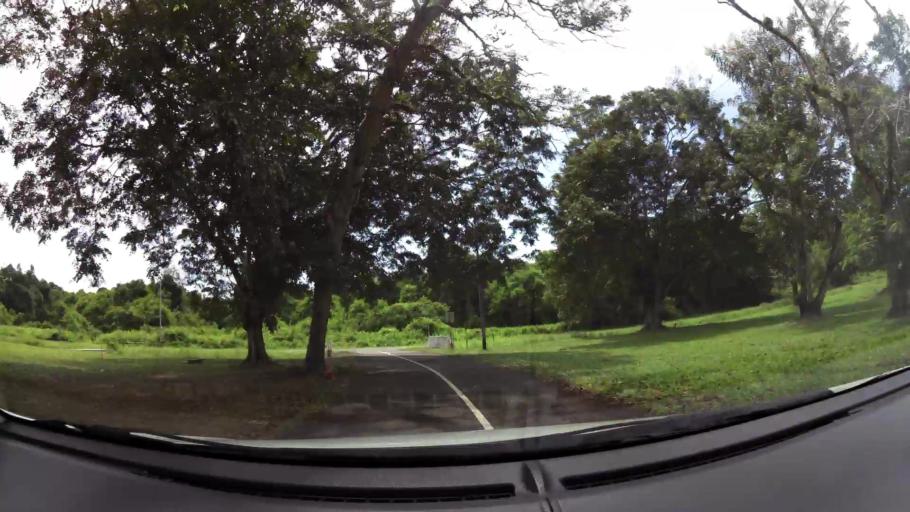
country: BN
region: Belait
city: Seria
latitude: 4.5930
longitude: 114.2838
